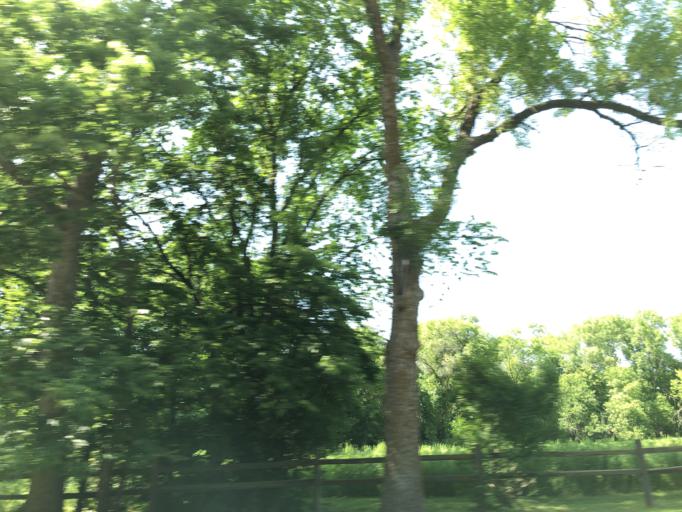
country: US
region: Minnesota
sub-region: Douglas County
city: Alexandria
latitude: 45.9402
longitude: -95.3776
